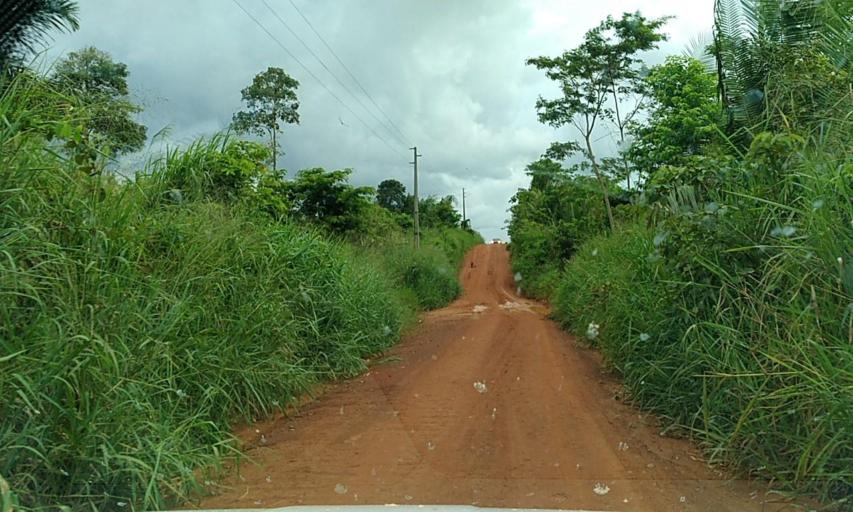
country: BR
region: Para
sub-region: Altamira
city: Altamira
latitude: -3.3279
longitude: -52.6835
